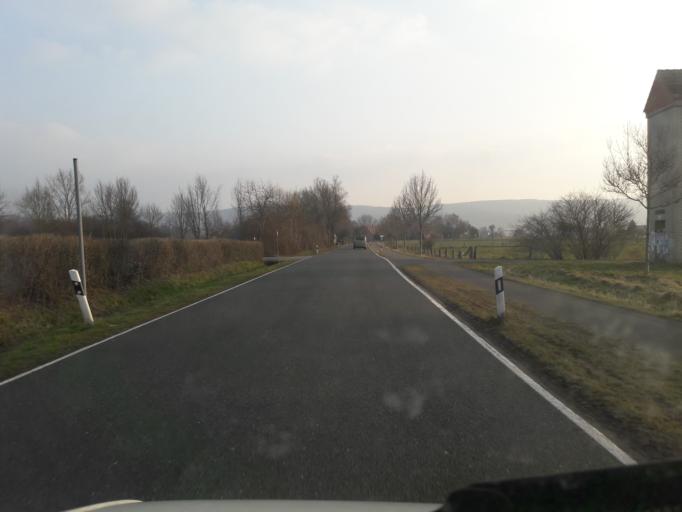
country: DE
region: North Rhine-Westphalia
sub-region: Regierungsbezirk Detmold
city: Huellhorst
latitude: 52.3291
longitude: 8.6675
